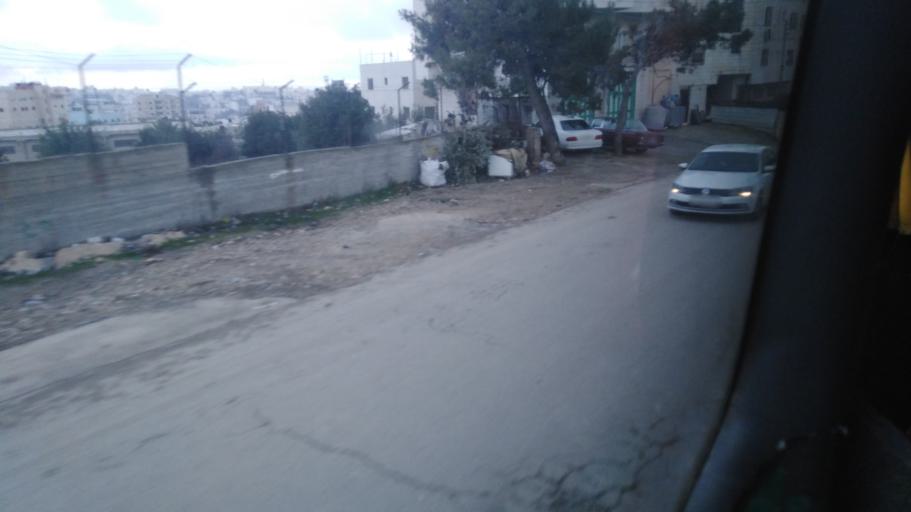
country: PS
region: West Bank
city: Hebron
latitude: 31.5278
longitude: 35.0783
